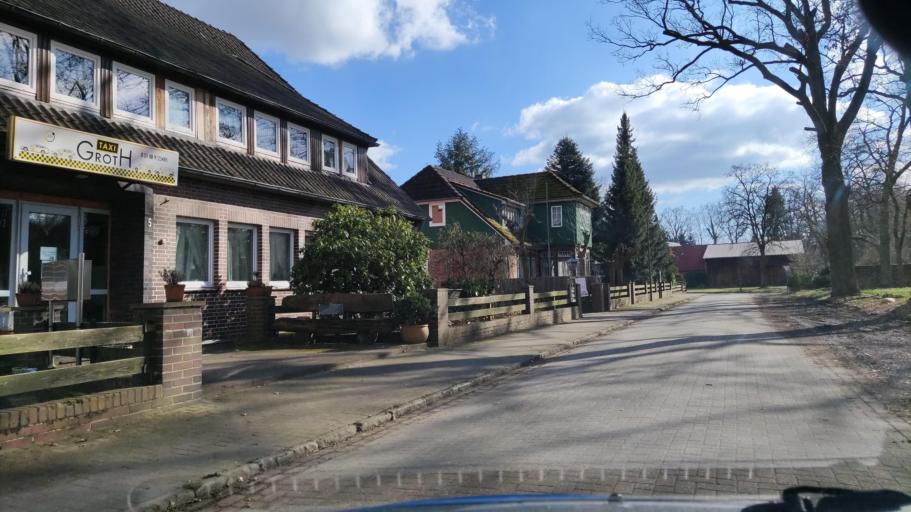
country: DE
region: Lower Saxony
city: Eldingen
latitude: 52.7024
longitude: 10.3467
